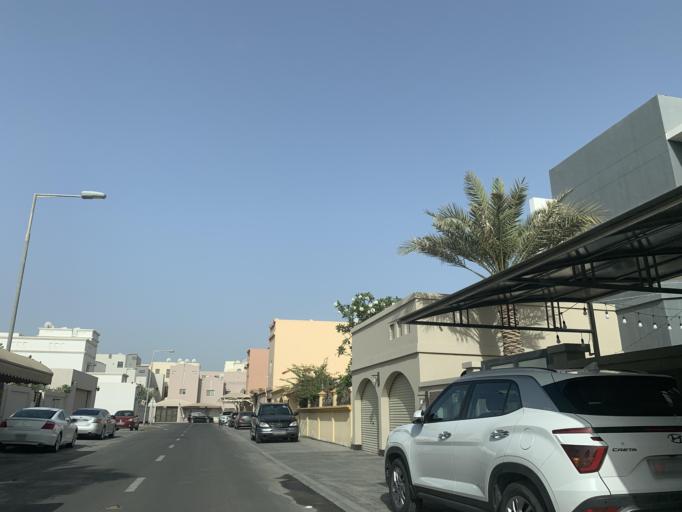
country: BH
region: Northern
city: Ar Rifa'
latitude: 26.1444
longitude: 50.5836
